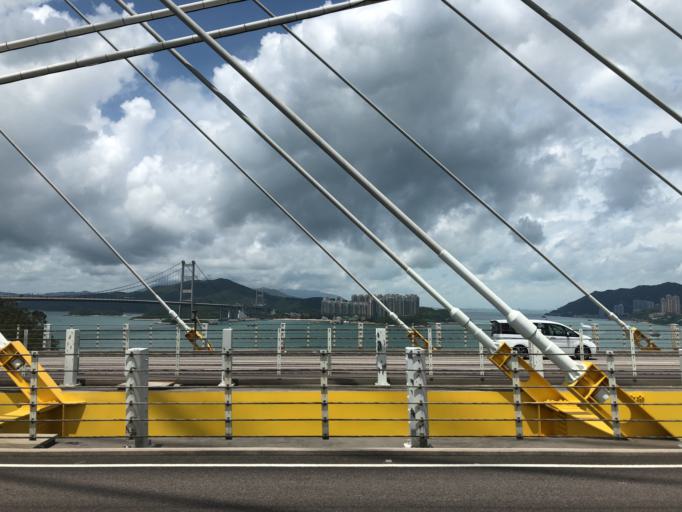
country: HK
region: Tsuen Wan
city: Tsuen Wan
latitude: 22.3612
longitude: 114.0814
